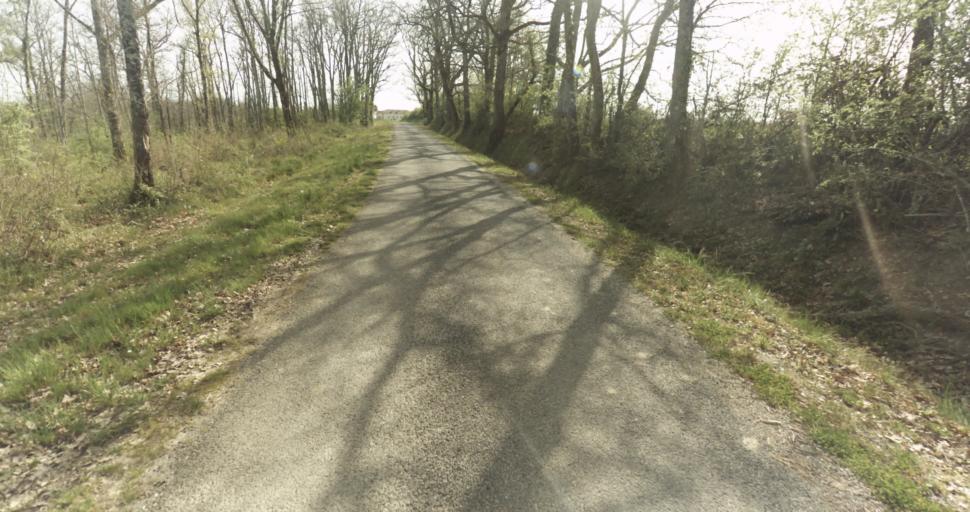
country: FR
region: Midi-Pyrenees
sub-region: Departement du Tarn-et-Garonne
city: Cazes-Mondenard
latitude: 44.1603
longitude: 1.1629
